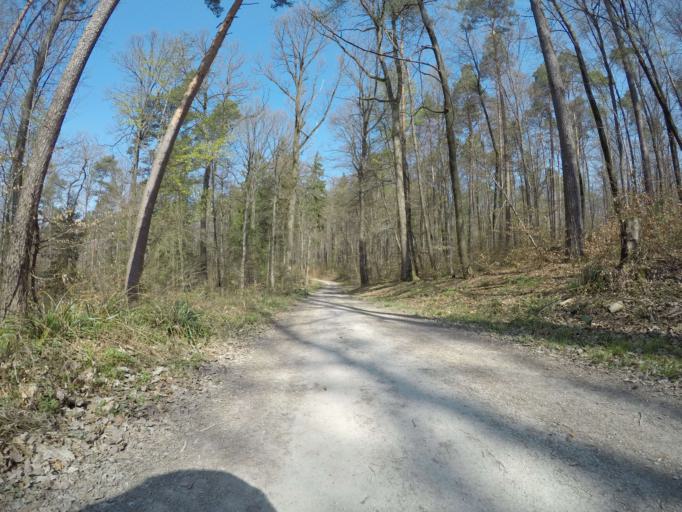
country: DE
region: Baden-Wuerttemberg
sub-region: Tuebingen Region
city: Gomaringen
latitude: 48.4669
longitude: 9.1401
